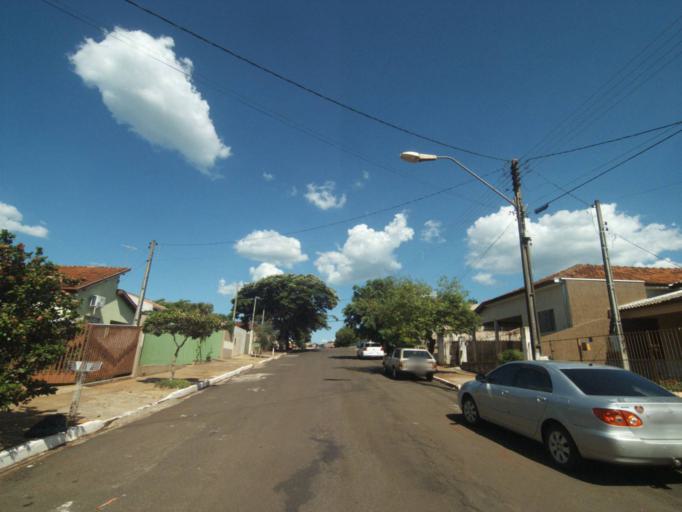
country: BR
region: Parana
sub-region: Sertanopolis
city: Sertanopolis
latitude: -23.0370
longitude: -50.8162
